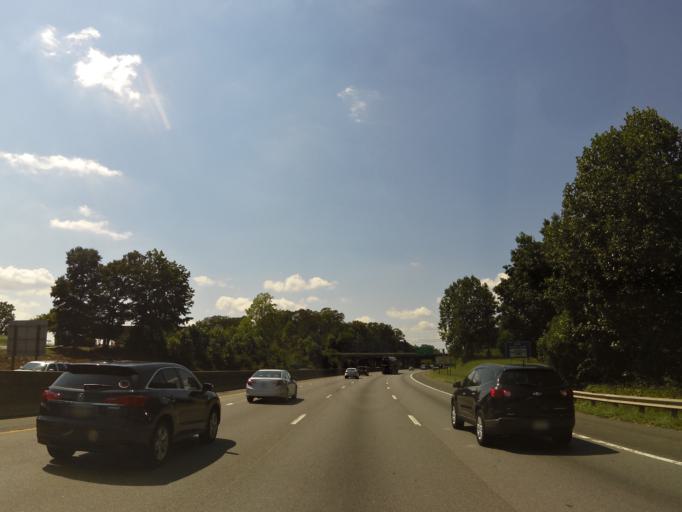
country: US
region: North Carolina
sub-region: Gaston County
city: Belmont
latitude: 35.2566
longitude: -81.0411
